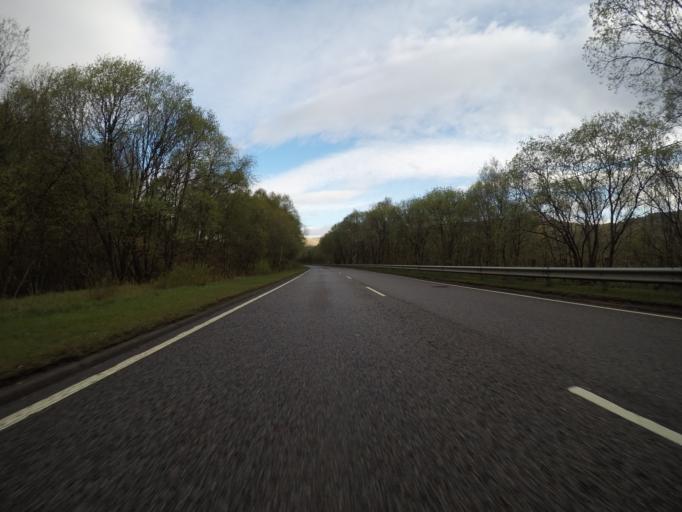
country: GB
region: Scotland
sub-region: Argyll and Bute
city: Garelochhead
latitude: 56.4003
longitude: -4.6377
